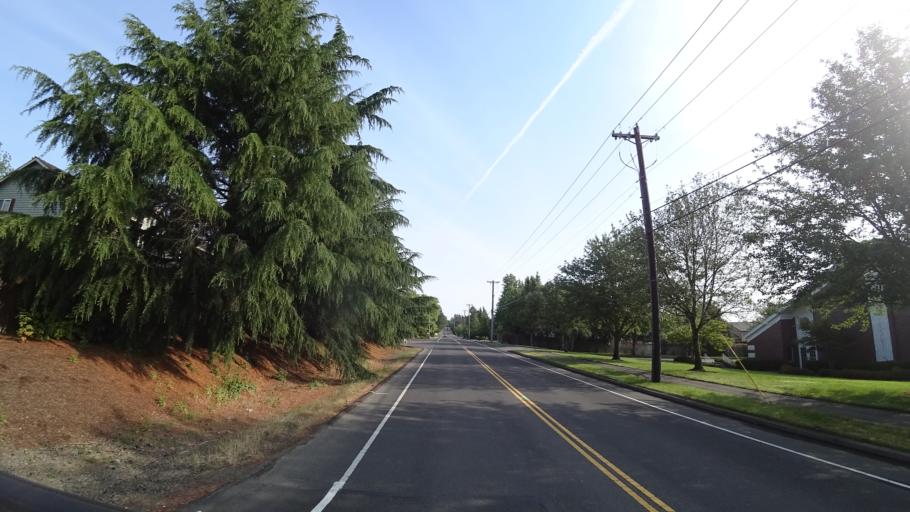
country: US
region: Oregon
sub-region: Clackamas County
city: Happy Valley
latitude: 45.4481
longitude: -122.5277
